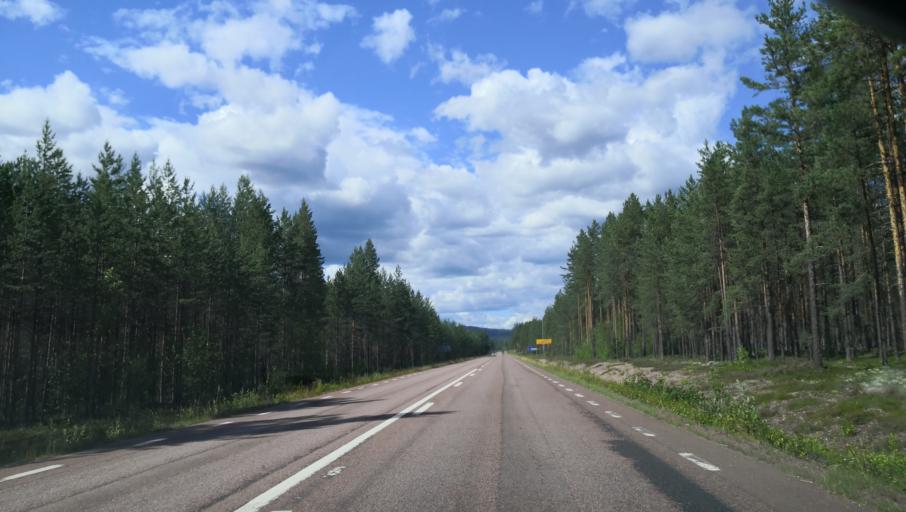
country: SE
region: Dalarna
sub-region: Alvdalens Kommun
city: AElvdalen
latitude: 61.2592
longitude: 14.0242
